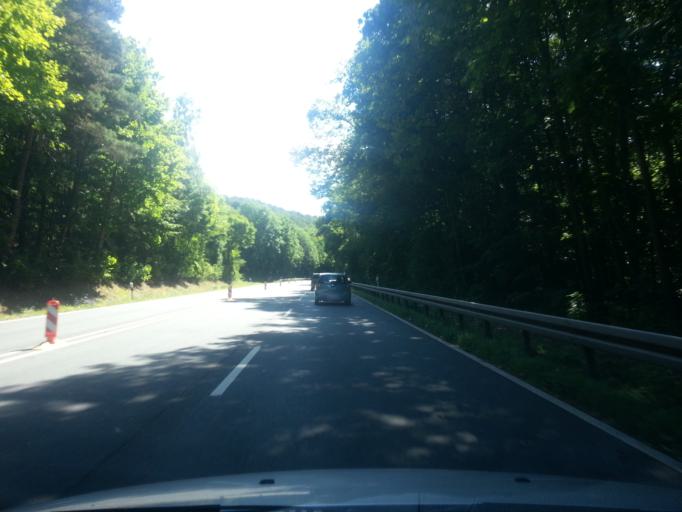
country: DE
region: Hesse
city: Gross-Umstadt
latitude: 49.8273
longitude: 8.9571
